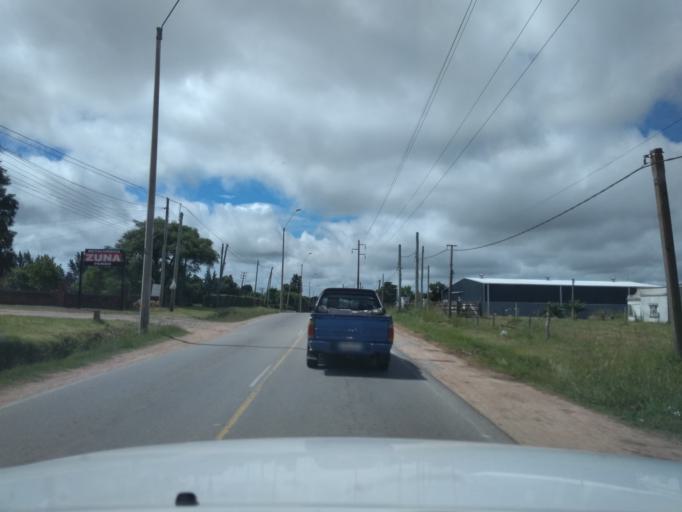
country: UY
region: Canelones
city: Pando
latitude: -34.7049
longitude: -55.9656
